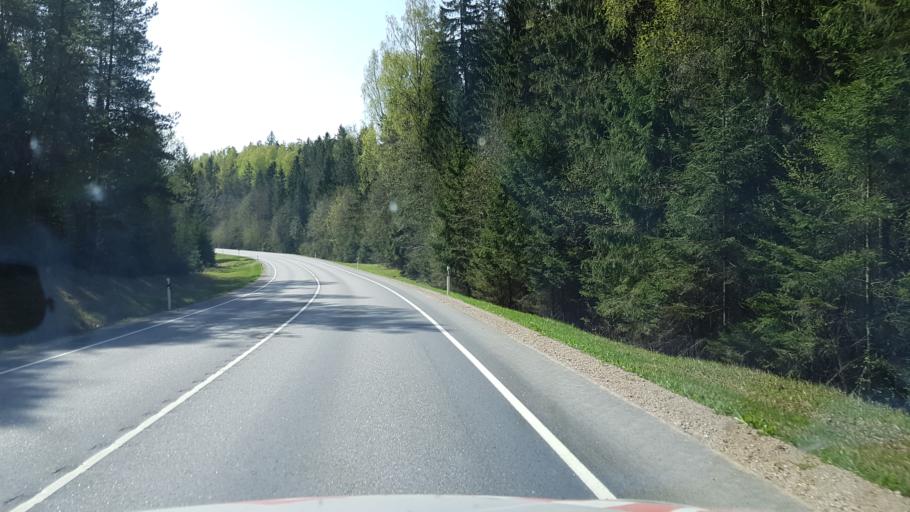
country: EE
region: Viljandimaa
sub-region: Karksi vald
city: Karksi-Nuia
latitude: 58.0787
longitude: 25.6149
